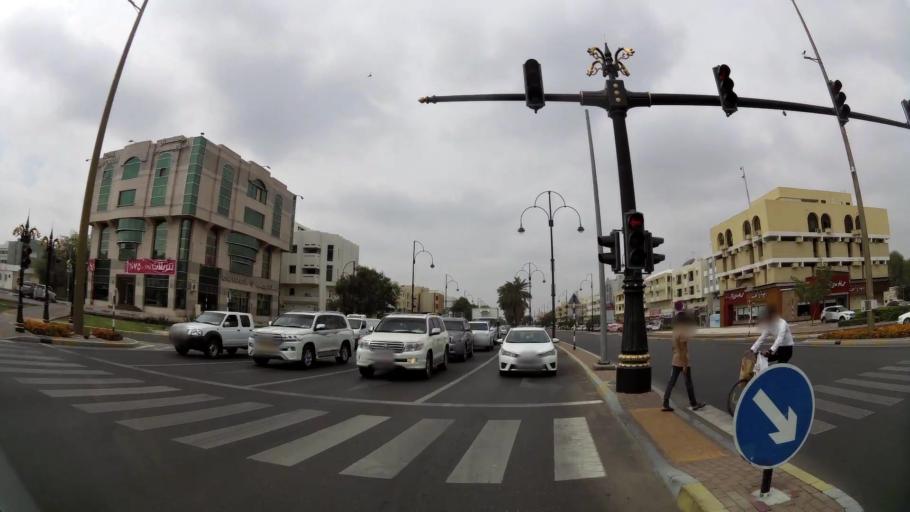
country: AE
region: Abu Dhabi
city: Al Ain
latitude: 24.2256
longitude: 55.7652
